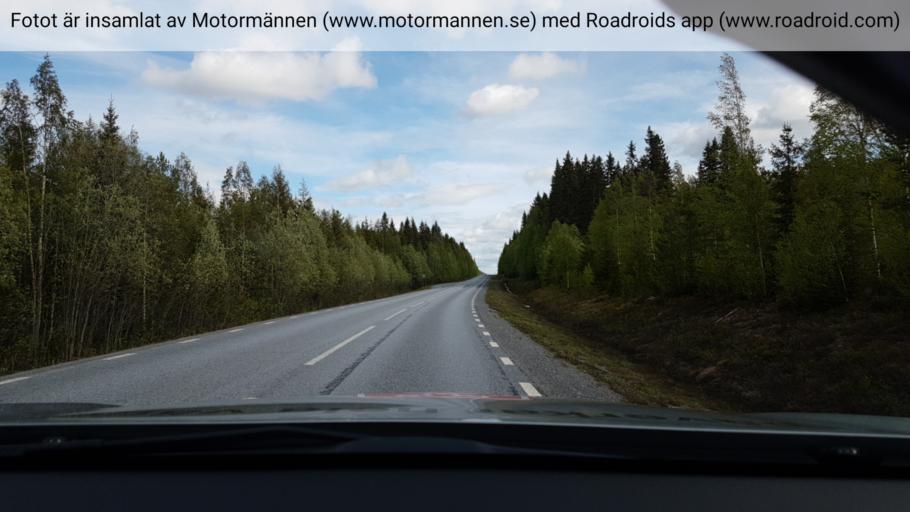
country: SE
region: Vaesterbotten
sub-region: Lycksele Kommun
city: Lycksele
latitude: 64.0528
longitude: 18.5546
